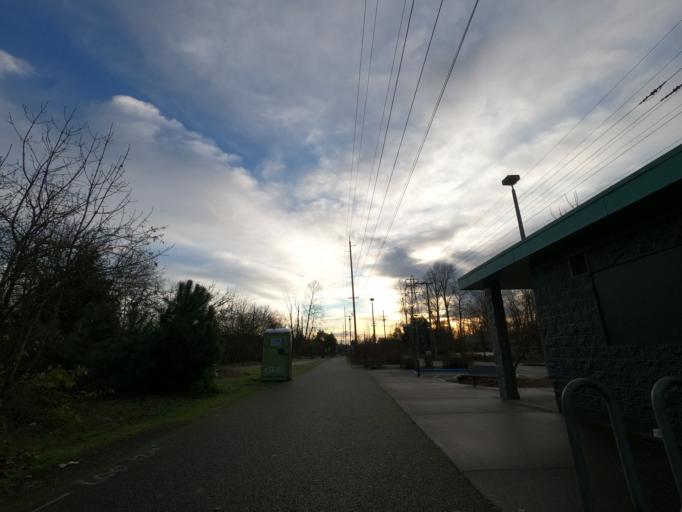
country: US
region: Oregon
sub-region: Clackamas County
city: Milwaukie
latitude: 45.4621
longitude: -122.6179
